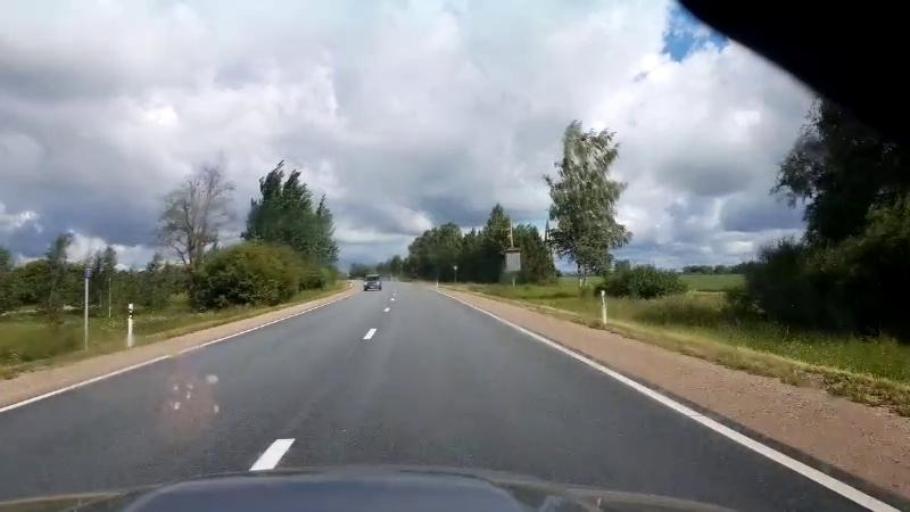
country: LV
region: Lecava
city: Iecava
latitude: 56.5229
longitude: 24.1723
